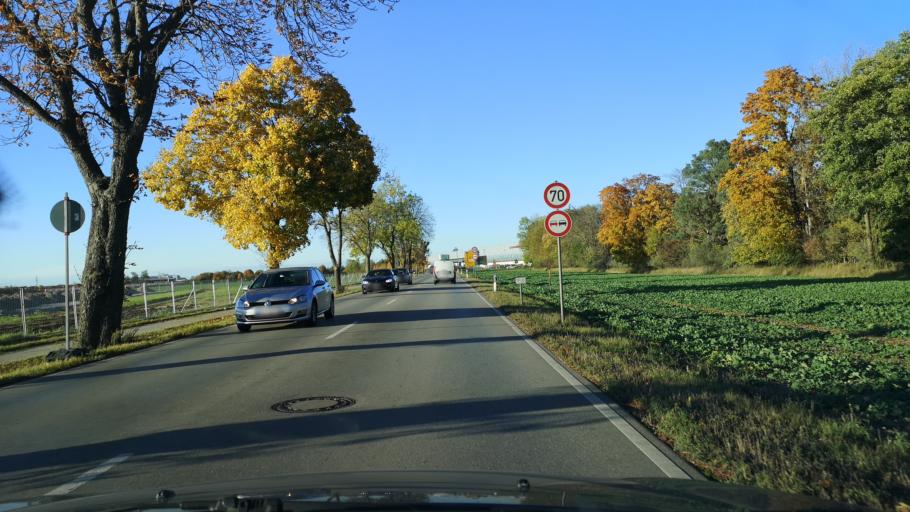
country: DE
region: Bavaria
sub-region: Upper Bavaria
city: Kirchheim bei Muenchen
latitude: 48.1578
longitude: 11.7848
